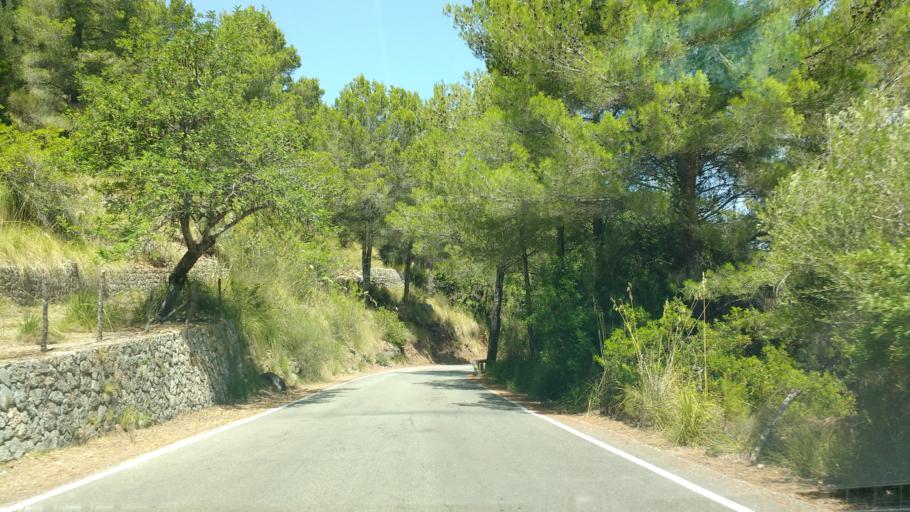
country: ES
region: Balearic Islands
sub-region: Illes Balears
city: Escorca
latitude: 39.8413
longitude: 2.7954
